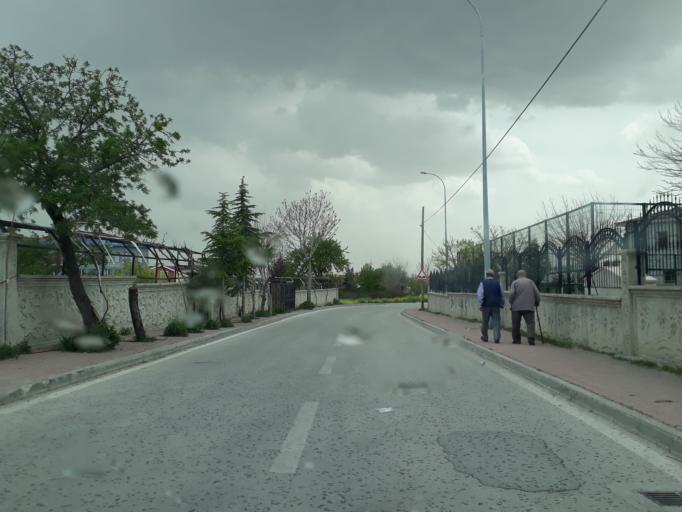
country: TR
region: Konya
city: Sille
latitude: 37.9200
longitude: 32.4628
